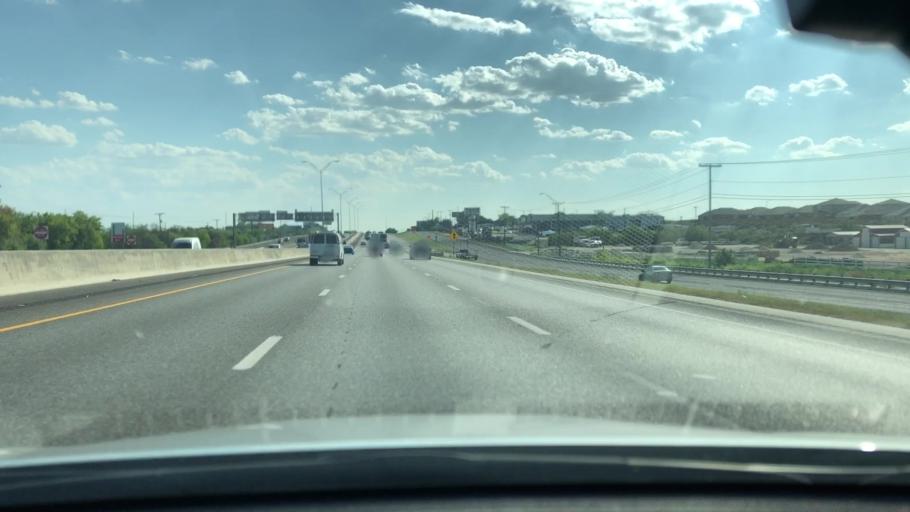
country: US
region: Texas
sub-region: Guadalupe County
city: Northcliff
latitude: 29.6514
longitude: -98.1929
